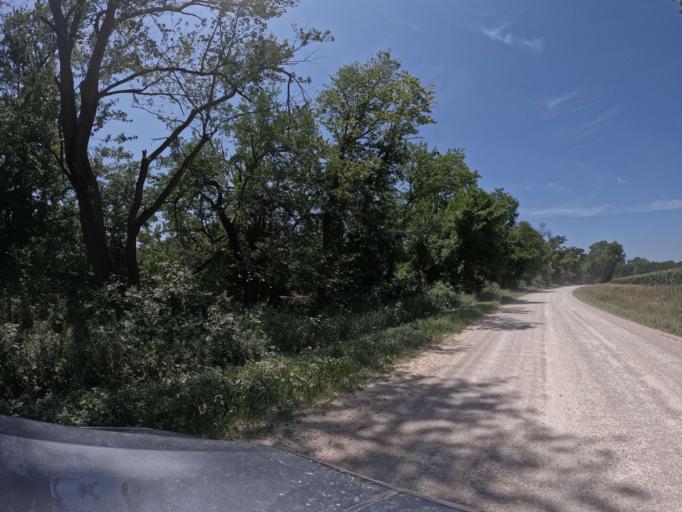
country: US
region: Iowa
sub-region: Henry County
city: Mount Pleasant
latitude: 40.9326
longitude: -91.6031
